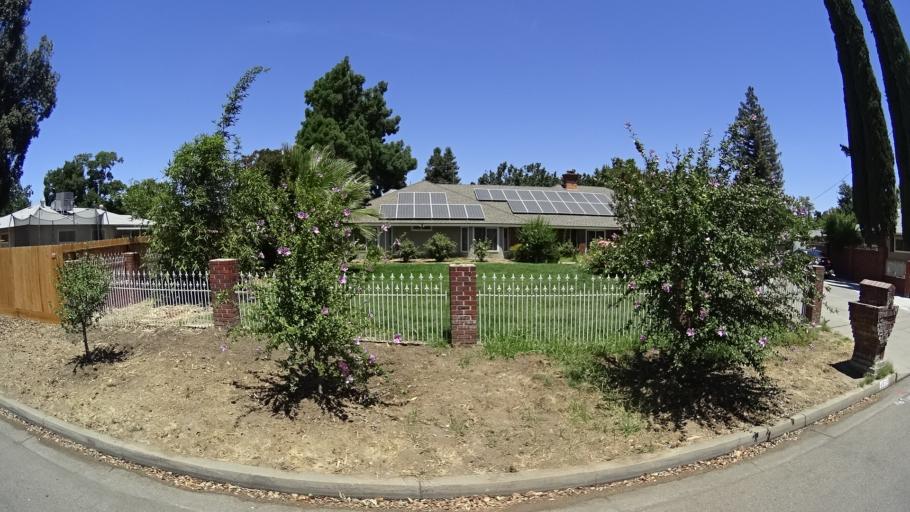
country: US
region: California
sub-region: Fresno County
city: Tarpey Village
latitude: 36.7972
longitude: -119.7491
